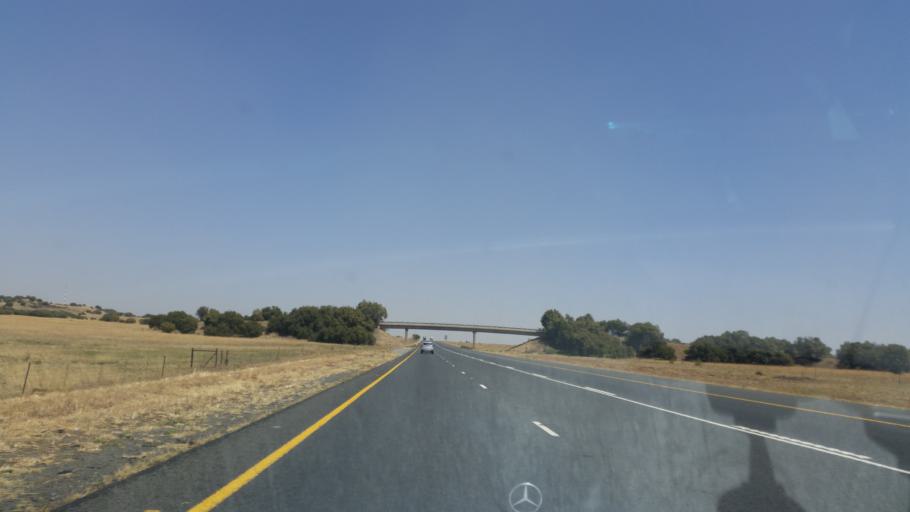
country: ZA
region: Orange Free State
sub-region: Lejweleputswa District Municipality
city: Winburg
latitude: -28.6955
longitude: 26.8071
